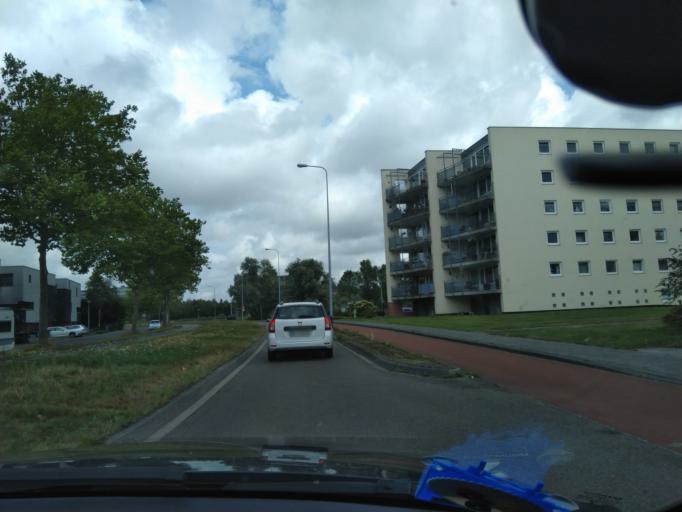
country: NL
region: Groningen
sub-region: Gemeente Groningen
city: Groningen
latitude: 53.2230
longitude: 6.5188
